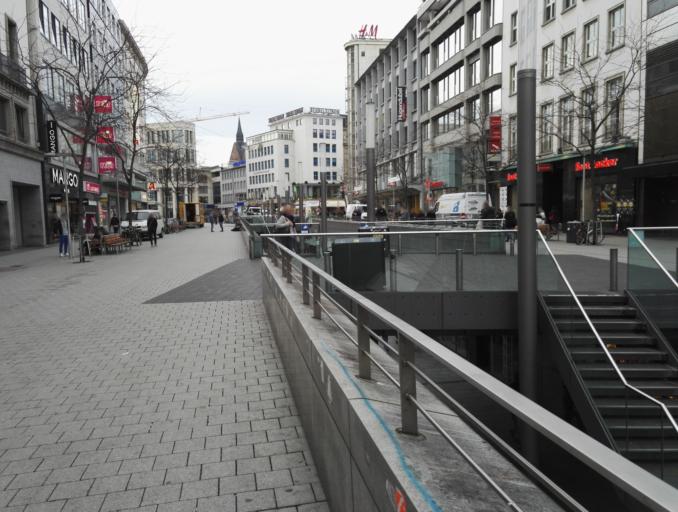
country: DE
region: Lower Saxony
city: Hannover
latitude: 52.3753
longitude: 9.7396
